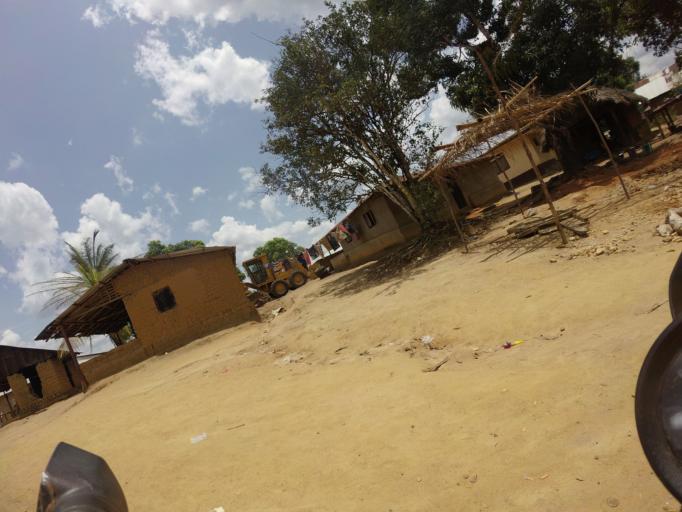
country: SL
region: Southern Province
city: Zimmi
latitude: 7.2199
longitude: -11.1764
